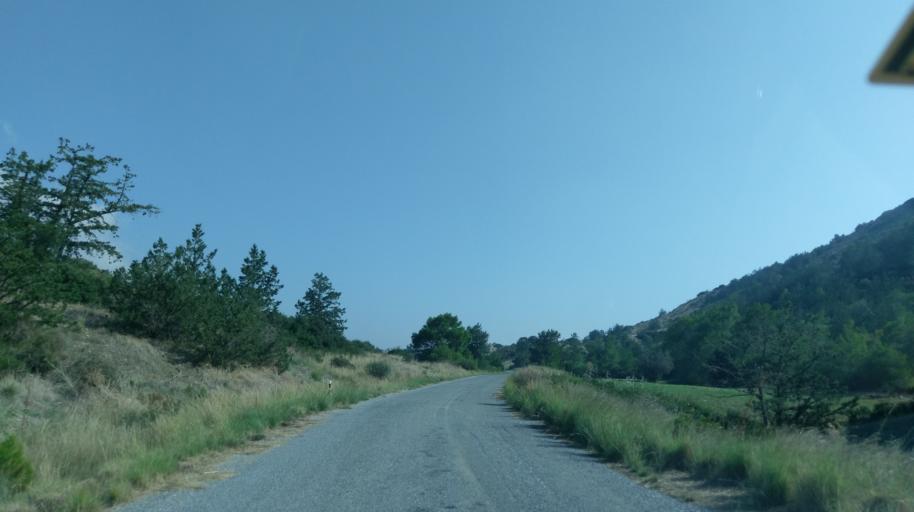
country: CY
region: Ammochostos
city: Lefkonoiko
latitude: 35.3198
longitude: 33.6607
